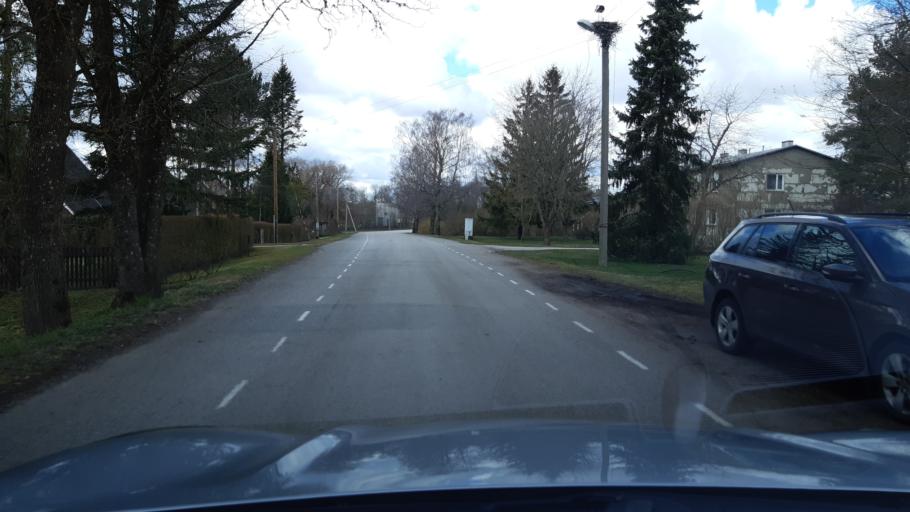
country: EE
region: Raplamaa
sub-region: Kehtna vald
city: Kehtna
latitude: 59.0415
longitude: 25.1231
